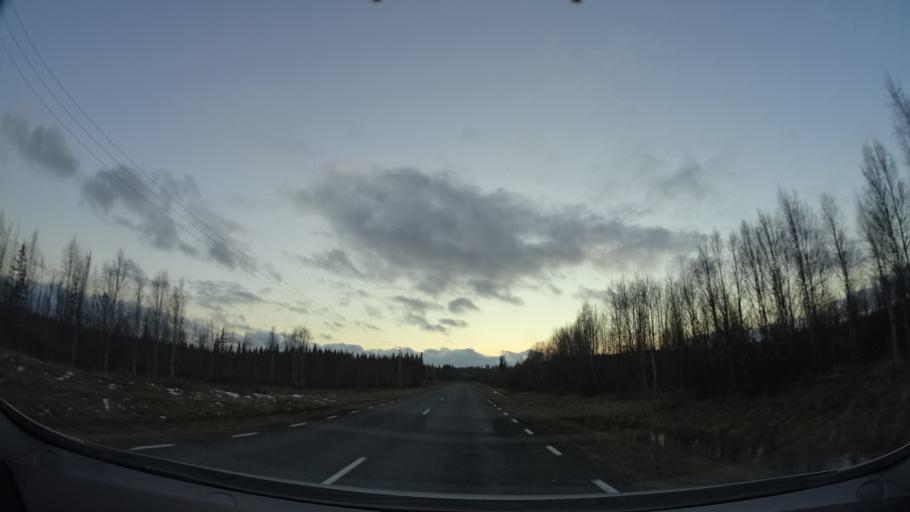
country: SE
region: Vaesterbotten
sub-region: Lycksele Kommun
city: Soderfors
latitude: 64.4623
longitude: 18.1576
